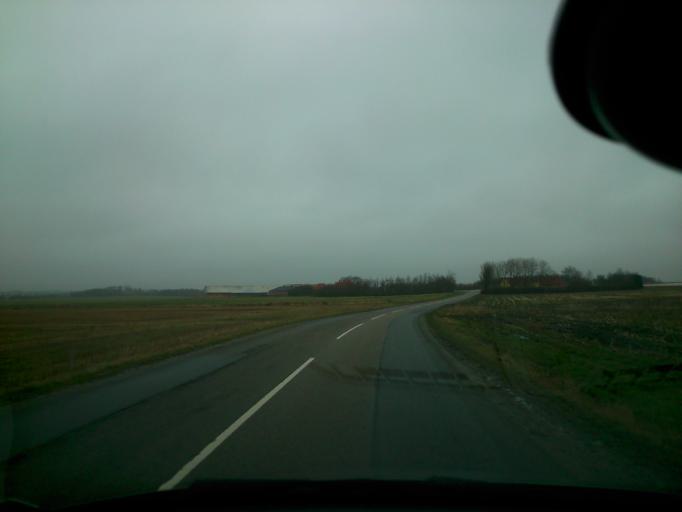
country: DK
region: Central Jutland
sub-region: Ringkobing-Skjern Kommune
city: Ringkobing
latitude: 56.0982
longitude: 8.4090
